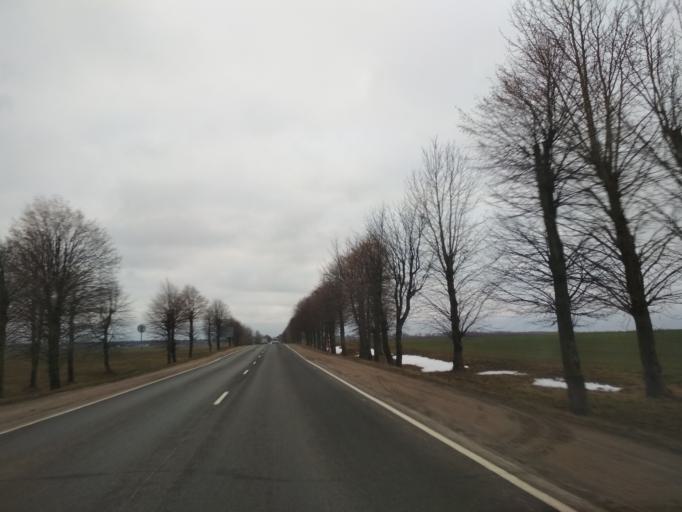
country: BY
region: Minsk
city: Blon'
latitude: 53.5416
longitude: 28.1663
